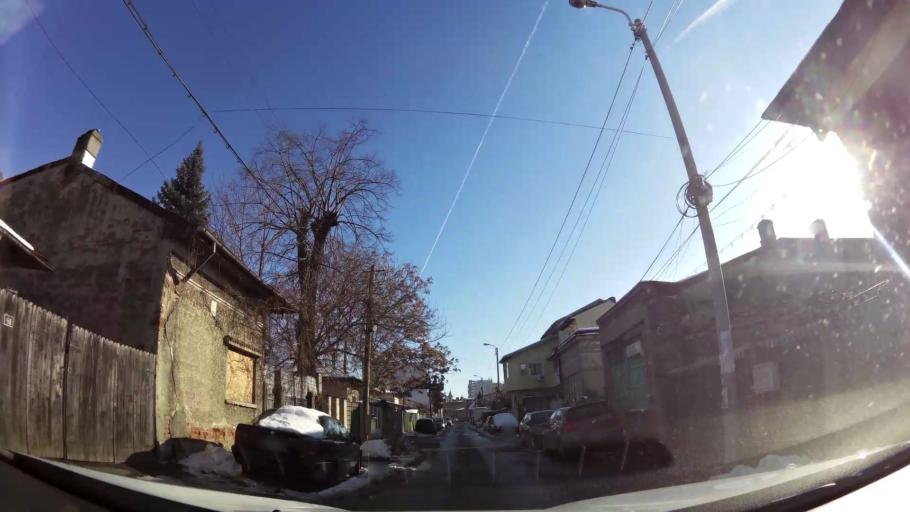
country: RO
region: Bucuresti
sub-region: Municipiul Bucuresti
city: Bucuresti
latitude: 44.4106
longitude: 26.0931
